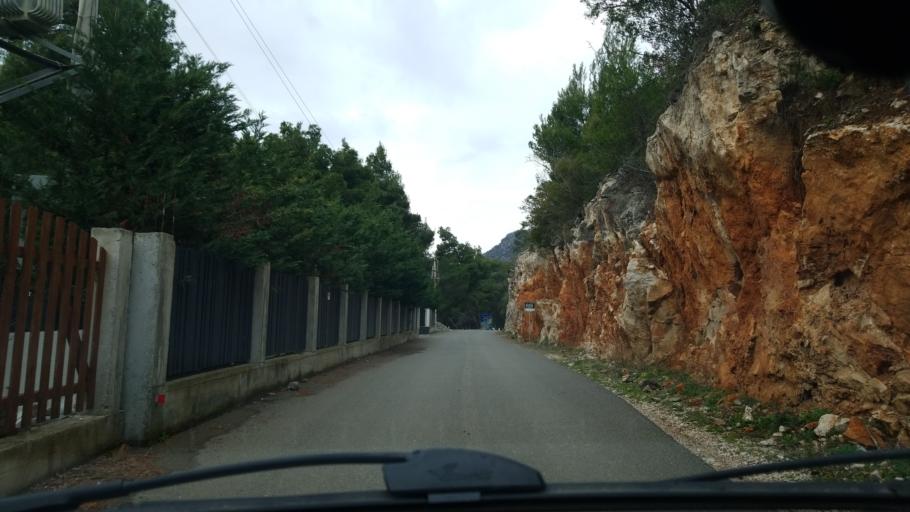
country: AL
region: Lezhe
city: Shengjin
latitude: 41.8209
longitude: 19.5626
